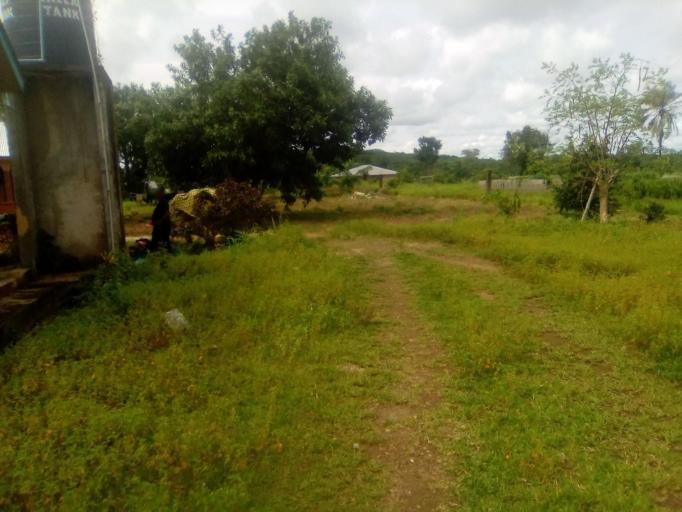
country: SL
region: Southern Province
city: Moyamba
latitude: 8.1460
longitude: -12.4317
